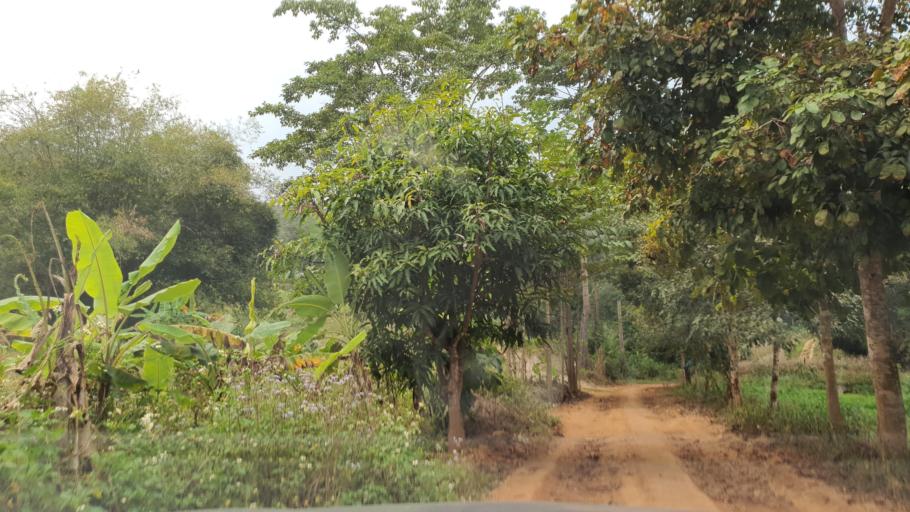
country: TH
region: Chiang Mai
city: Mae Wang
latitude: 18.6550
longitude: 98.6554
